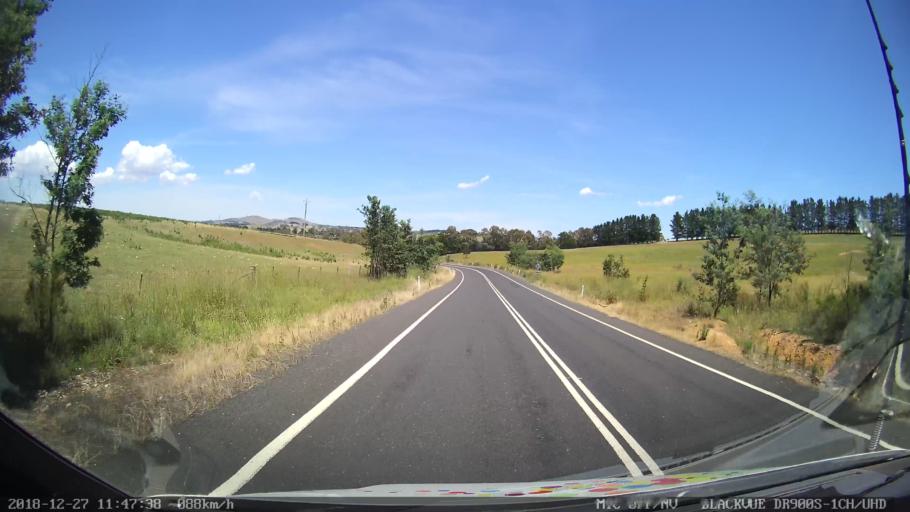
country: AU
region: New South Wales
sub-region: Bathurst Regional
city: Perthville
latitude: -33.5980
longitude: 149.4431
